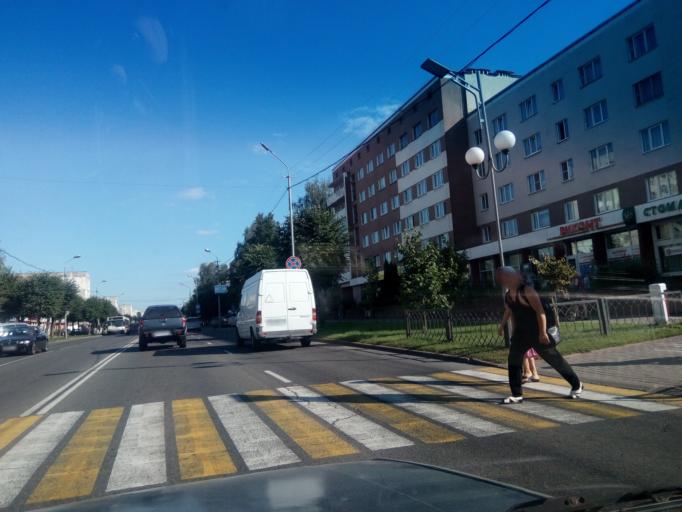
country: BY
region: Vitebsk
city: Navapolatsk
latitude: 55.5315
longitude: 28.6618
